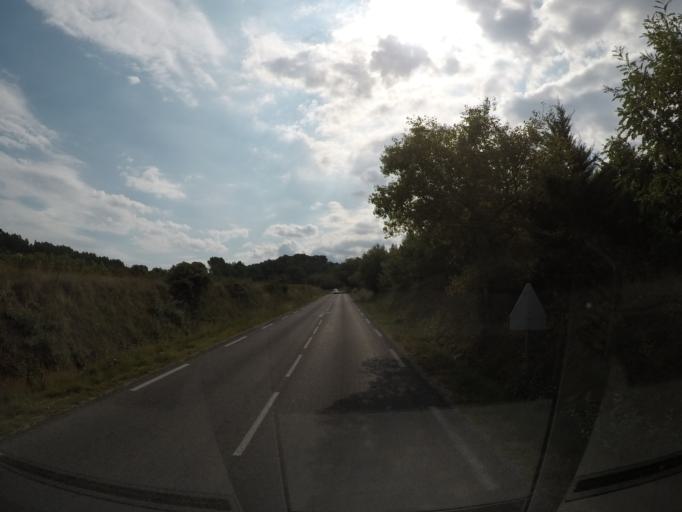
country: FR
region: Provence-Alpes-Cote d'Azur
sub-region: Departement du Vaucluse
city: Ansouis
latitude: 43.7295
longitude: 5.4892
